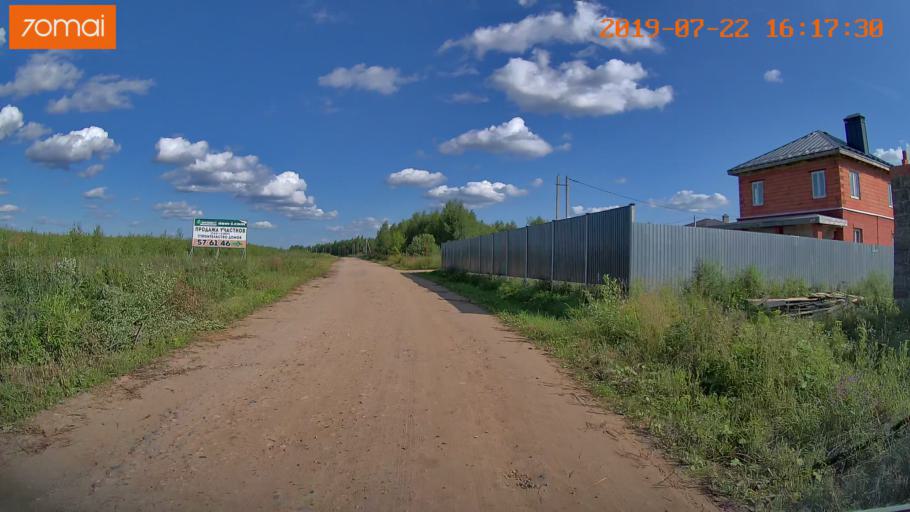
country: RU
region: Ivanovo
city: Novo-Talitsy
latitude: 57.0690
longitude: 40.8830
